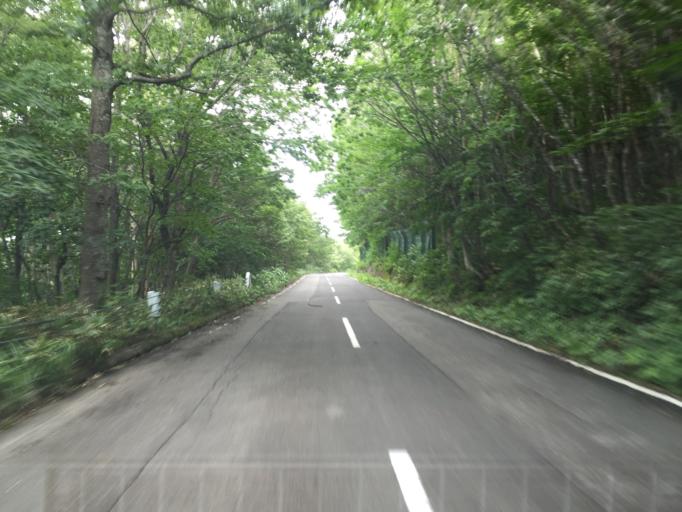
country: JP
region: Fukushima
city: Nihommatsu
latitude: 37.6524
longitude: 140.3098
